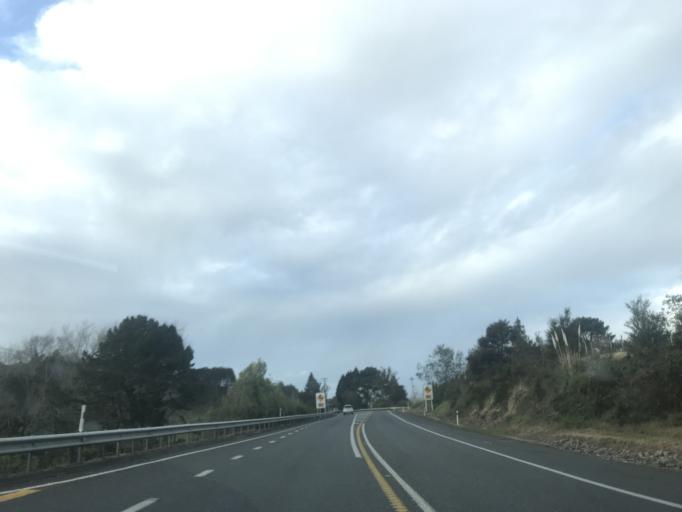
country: NZ
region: Bay of Plenty
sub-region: Western Bay of Plenty District
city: Katikati
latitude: -37.4918
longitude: 175.9282
